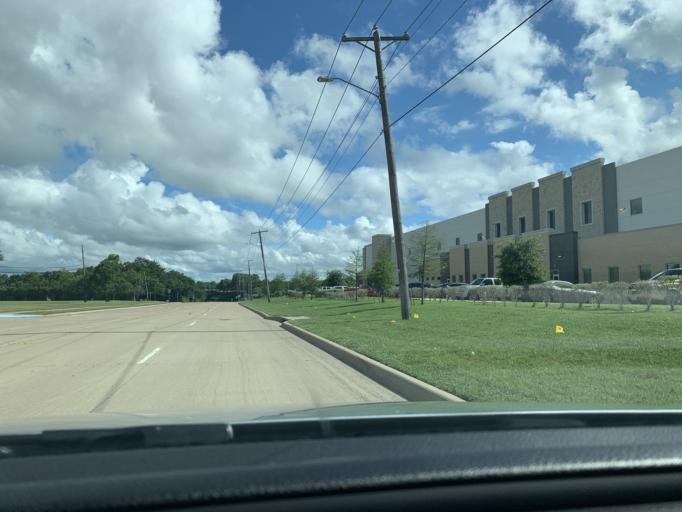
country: US
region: Texas
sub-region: Dallas County
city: Grand Prairie
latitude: 32.6719
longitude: -97.0310
